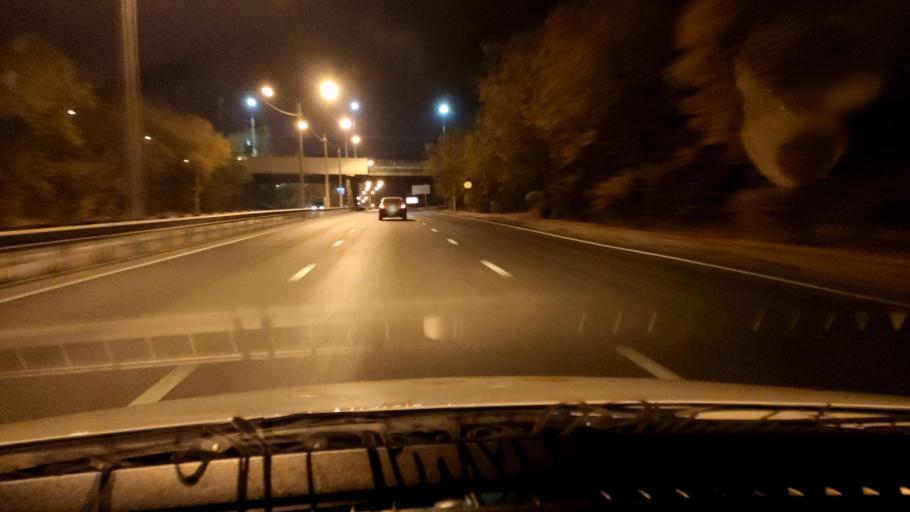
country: RU
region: Voronezj
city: Voronezh
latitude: 51.6530
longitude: 39.1362
